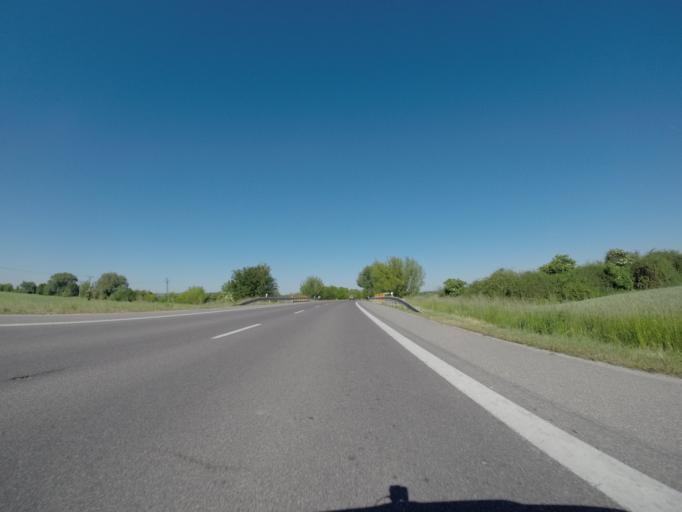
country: SK
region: Nitriansky
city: Banovce nad Bebravou
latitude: 48.5394
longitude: 18.1631
